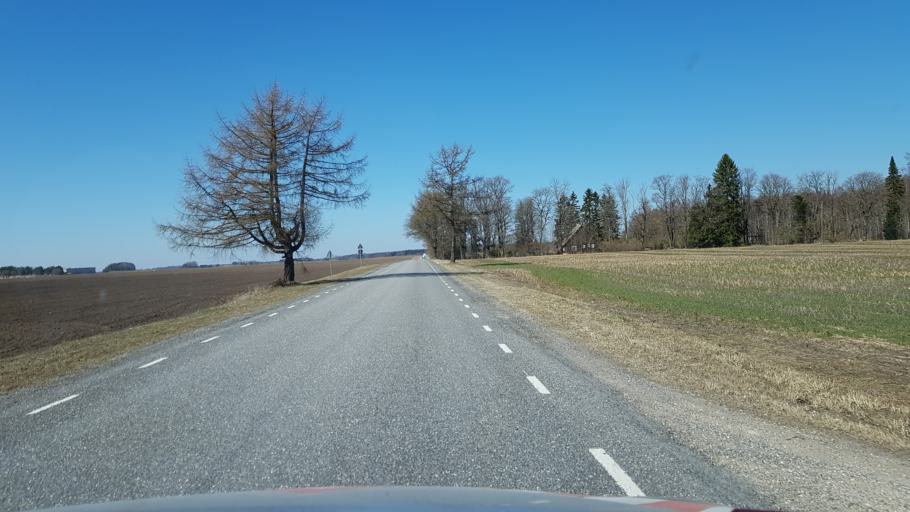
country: EE
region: Laeaene-Virumaa
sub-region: Rakke vald
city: Rakke
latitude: 58.9996
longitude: 26.2022
